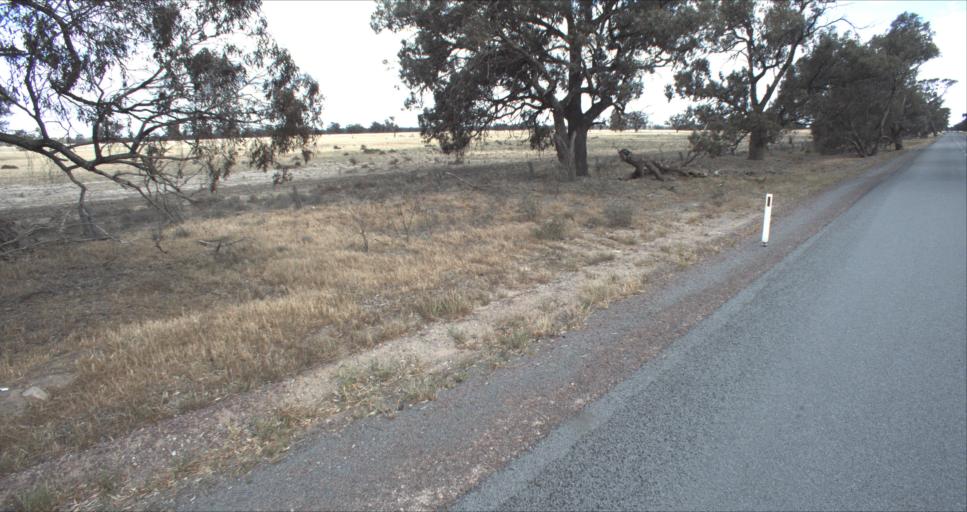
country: AU
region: New South Wales
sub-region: Leeton
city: Leeton
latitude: -34.6833
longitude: 146.3452
